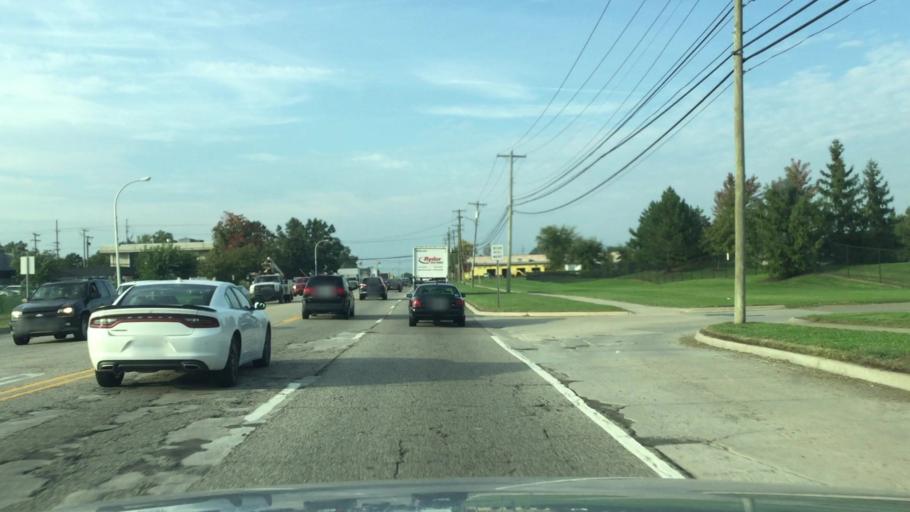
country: US
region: Michigan
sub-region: Oakland County
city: Madison Heights
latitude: 42.5092
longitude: -83.1059
